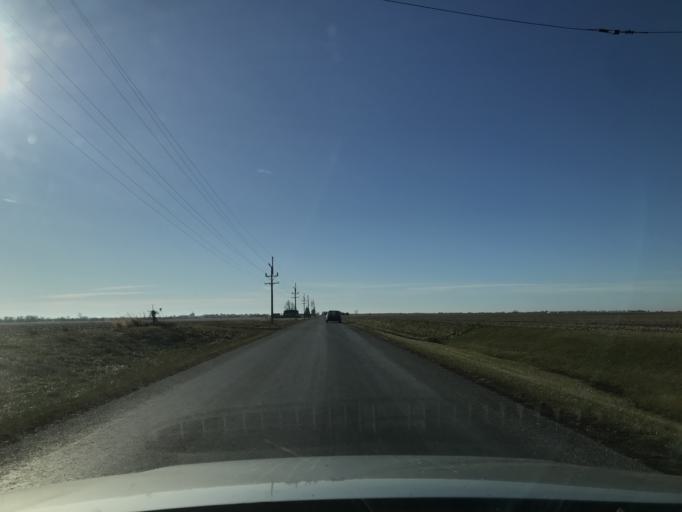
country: US
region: Illinois
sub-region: Hancock County
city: Carthage
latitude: 40.5036
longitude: -91.1776
